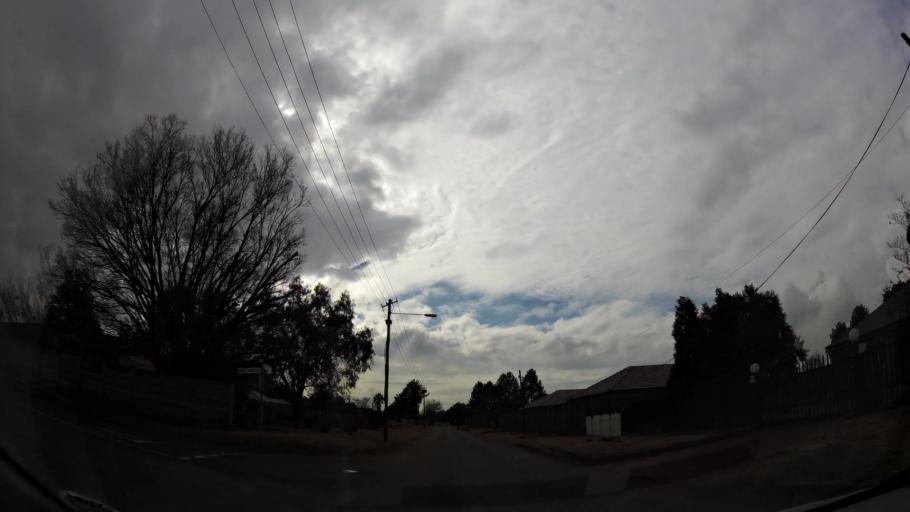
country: ZA
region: Gauteng
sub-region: Sedibeng District Municipality
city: Meyerton
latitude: -26.5852
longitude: 28.0018
